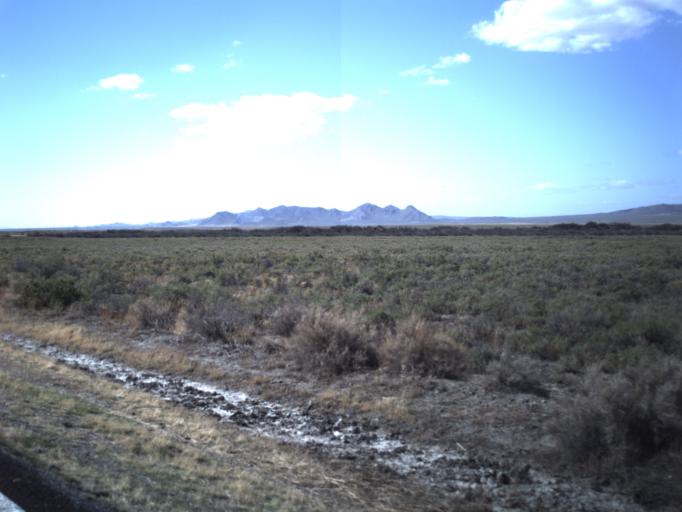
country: US
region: Utah
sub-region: Beaver County
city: Milford
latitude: 38.5515
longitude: -112.9912
